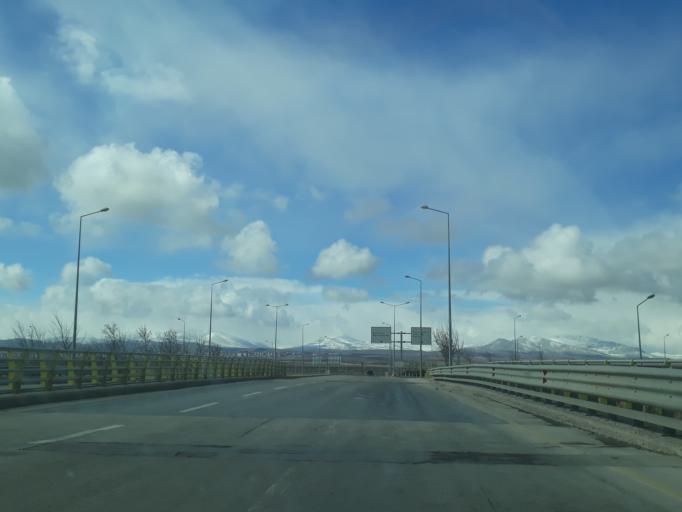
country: TR
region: Konya
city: Asagipinarbasi
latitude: 37.9903
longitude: 32.5954
